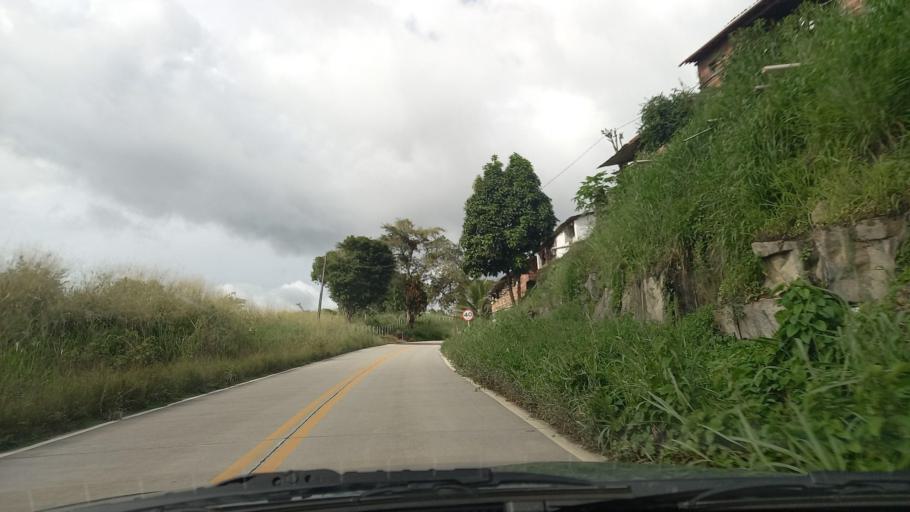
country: BR
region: Pernambuco
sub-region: Maraial
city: Maraial
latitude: -8.7908
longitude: -35.8833
